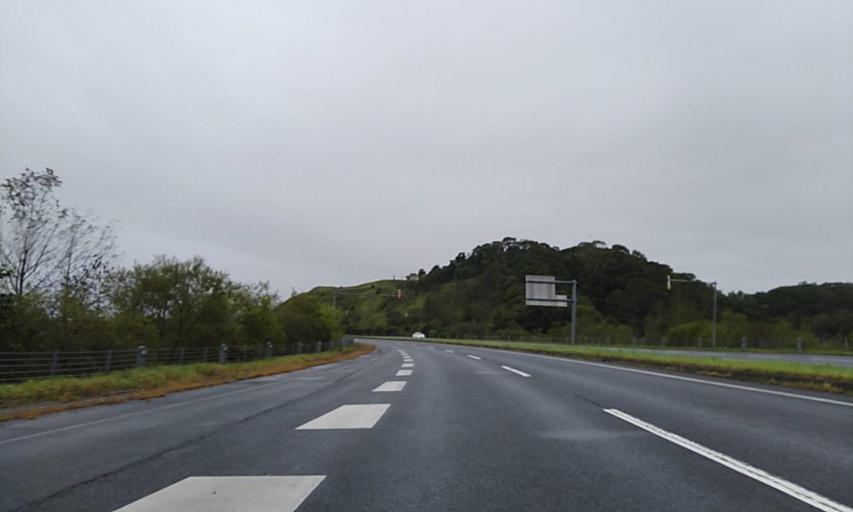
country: JP
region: Hokkaido
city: Kushiro
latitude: 43.0192
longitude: 144.2579
